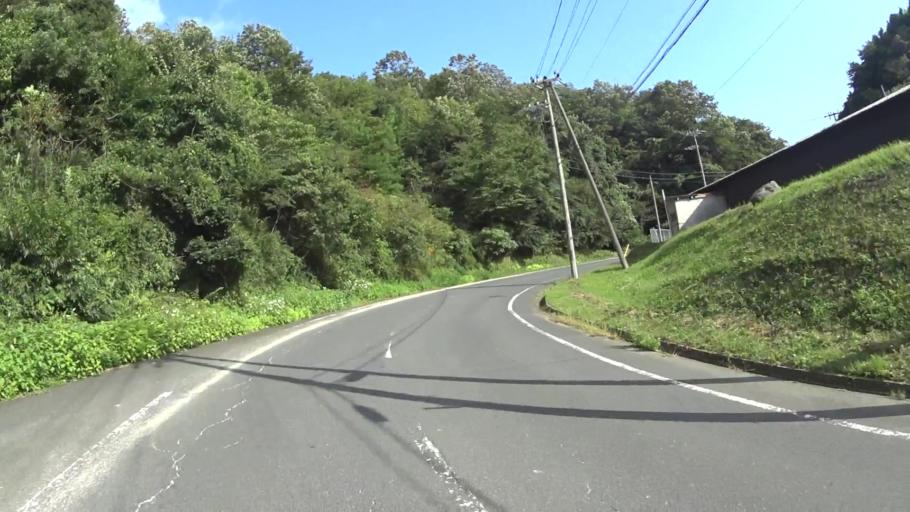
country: JP
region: Kyoto
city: Miyazu
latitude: 35.5735
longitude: 135.1111
